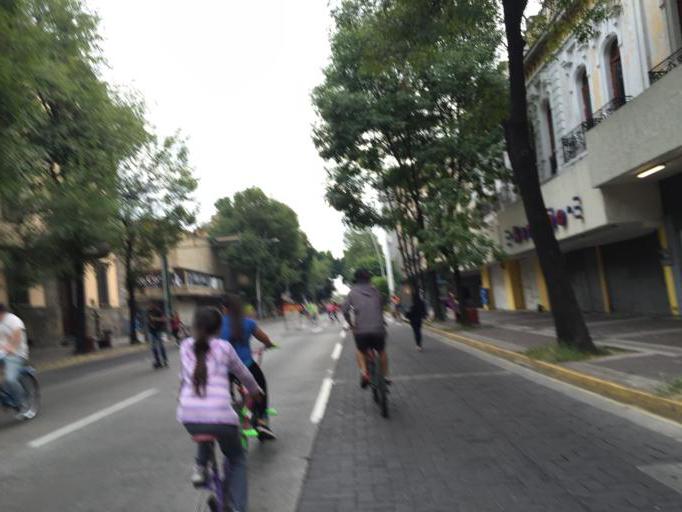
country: MX
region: Jalisco
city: Guadalajara
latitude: 20.6750
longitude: -103.3511
